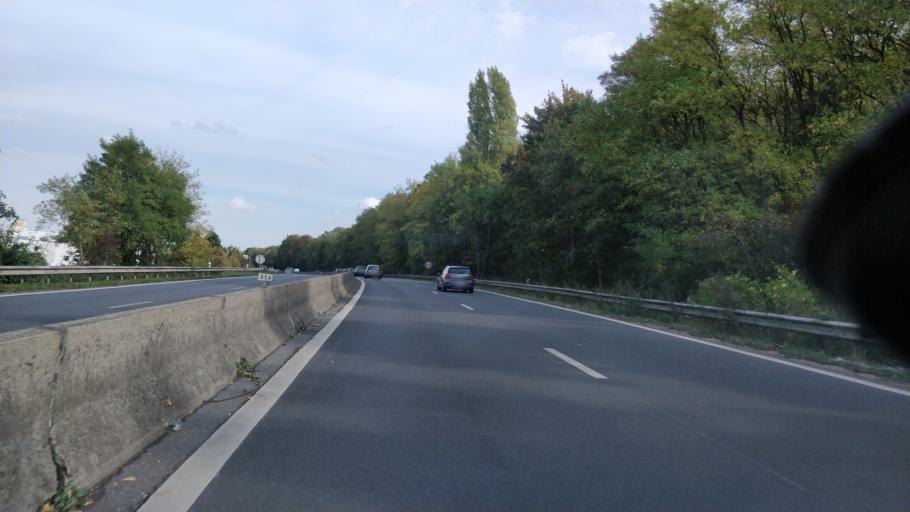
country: FR
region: Ile-de-France
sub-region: Departement de Seine-Saint-Denis
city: Coubron
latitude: 48.9333
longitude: 2.5899
